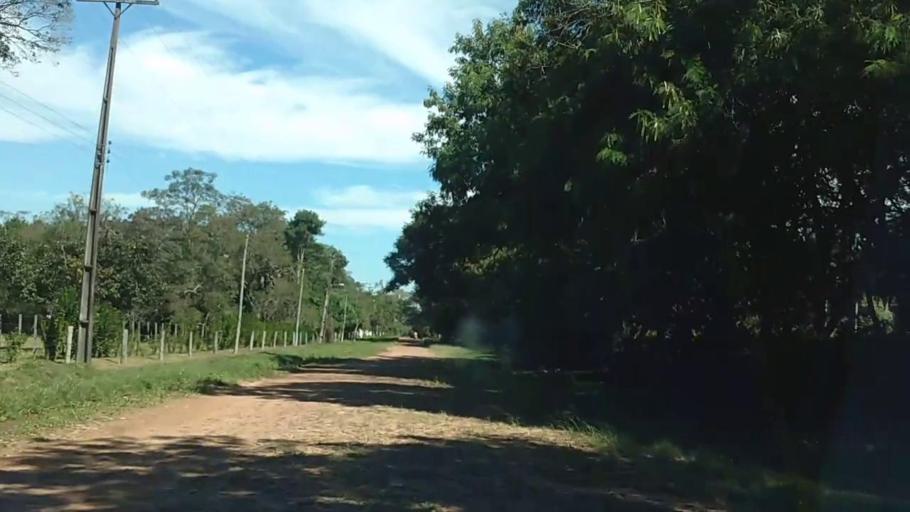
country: PY
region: Cordillera
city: San Bernardino
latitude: -25.3267
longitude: -57.2643
